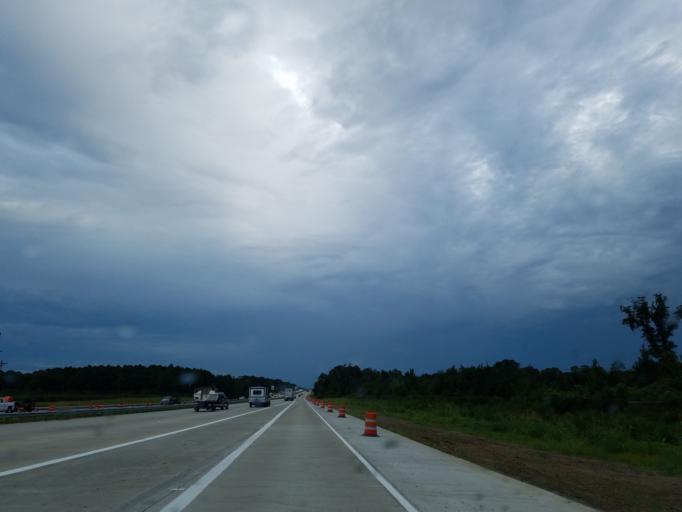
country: US
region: Georgia
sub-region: Dooly County
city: Vienna
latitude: 32.0831
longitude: -83.7636
